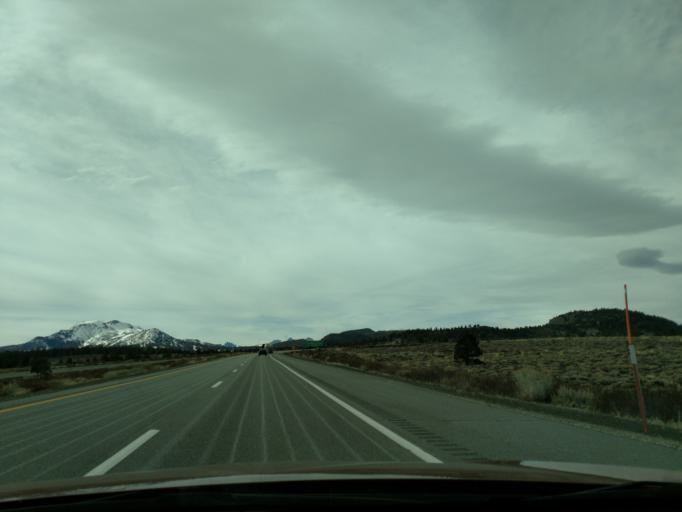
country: US
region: California
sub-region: Mono County
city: Mammoth Lakes
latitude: 37.6388
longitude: -118.9085
